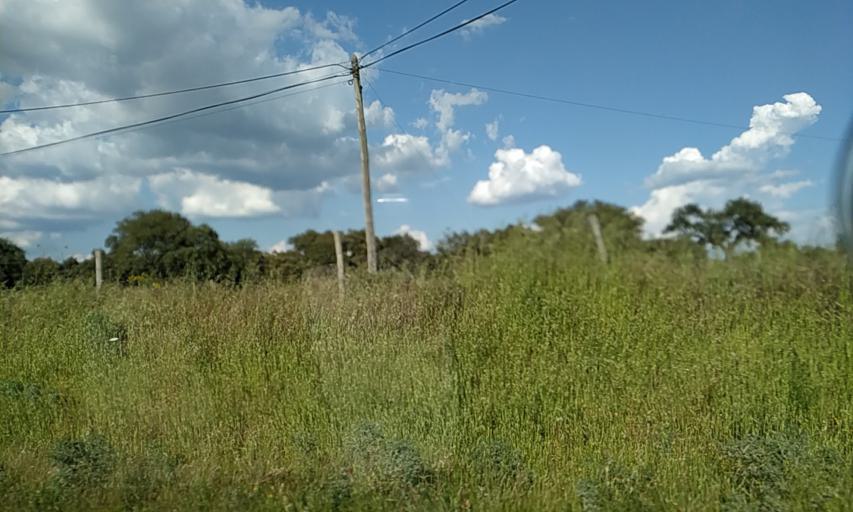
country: PT
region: Portalegre
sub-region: Portalegre
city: Urra
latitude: 39.1690
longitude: -7.4538
